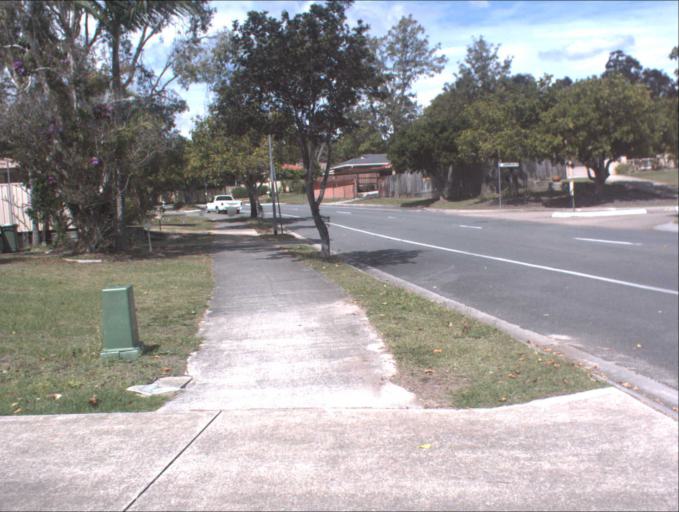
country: AU
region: Queensland
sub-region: Logan
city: Park Ridge South
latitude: -27.6945
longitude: 153.0195
